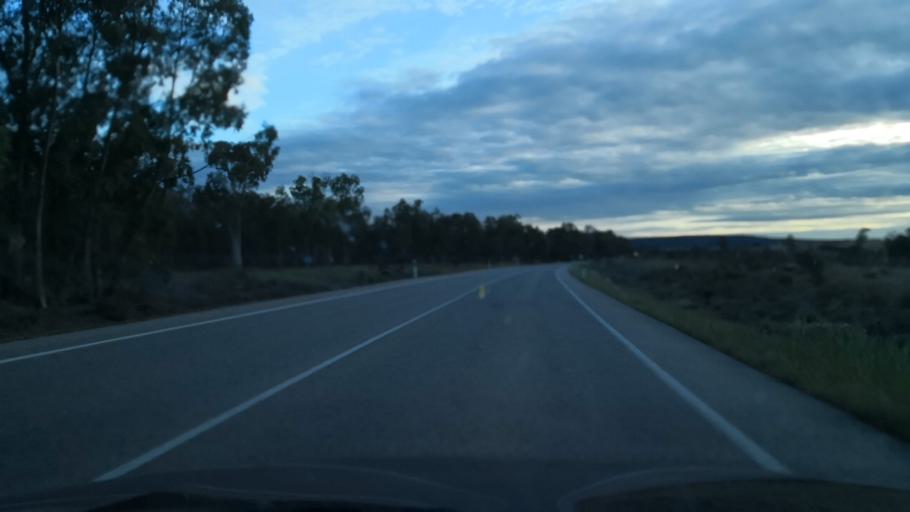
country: ES
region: Extremadura
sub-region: Provincia de Caceres
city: Malpartida de Caceres
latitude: 39.3310
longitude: -6.4869
